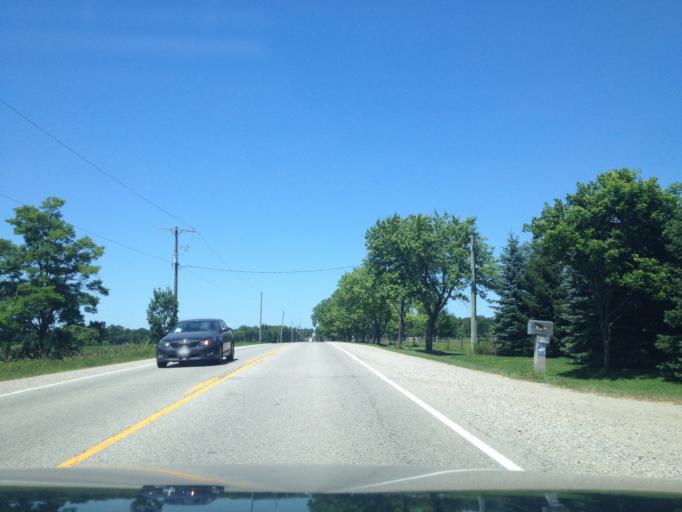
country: CA
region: Ontario
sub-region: Wellington County
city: Guelph
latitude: 43.6397
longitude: -80.2480
